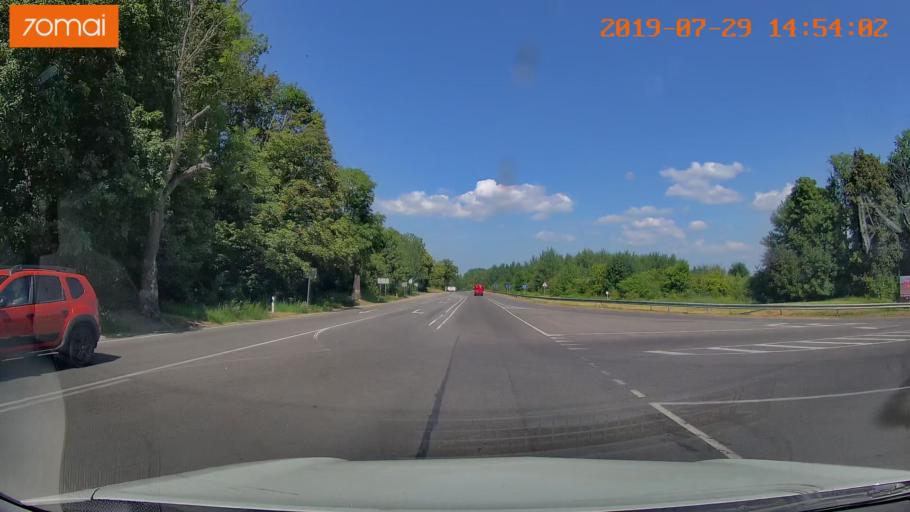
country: RU
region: Kaliningrad
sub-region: Gorod Kaliningrad
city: Baltiysk
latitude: 54.6705
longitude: 19.9218
